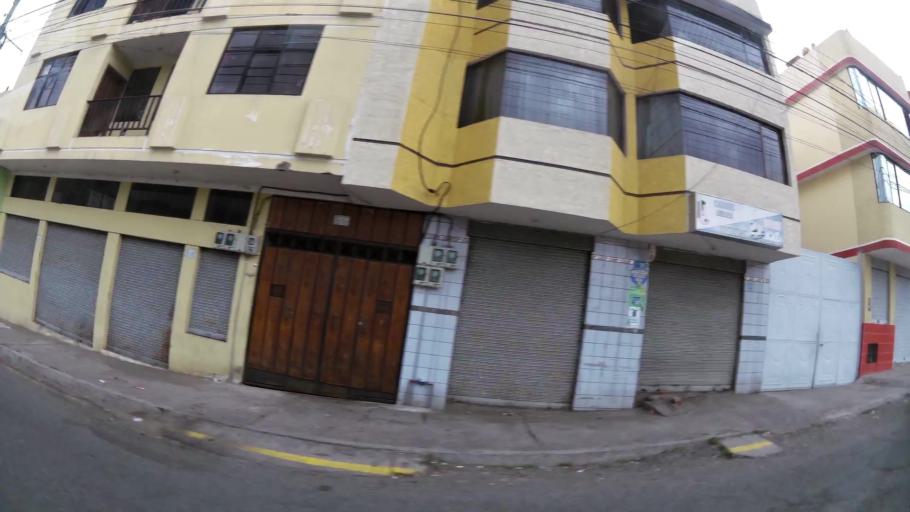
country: EC
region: Tungurahua
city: Ambato
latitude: -1.2300
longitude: -78.6188
